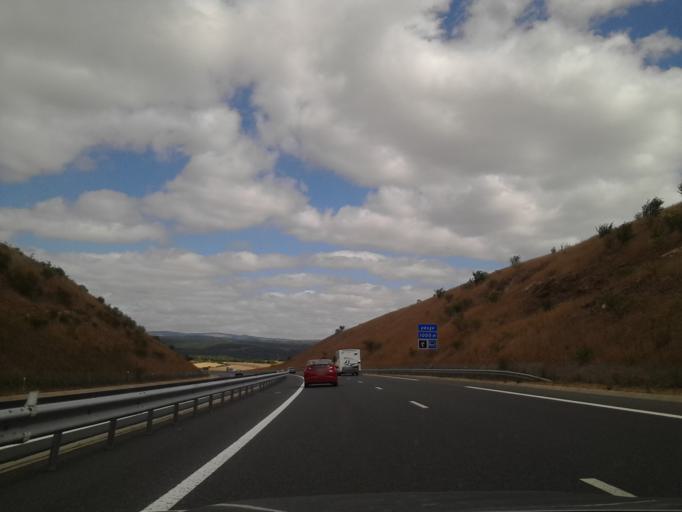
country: FR
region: Midi-Pyrenees
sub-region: Departement de l'Aveyron
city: Creissels
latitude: 44.1256
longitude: 3.0310
